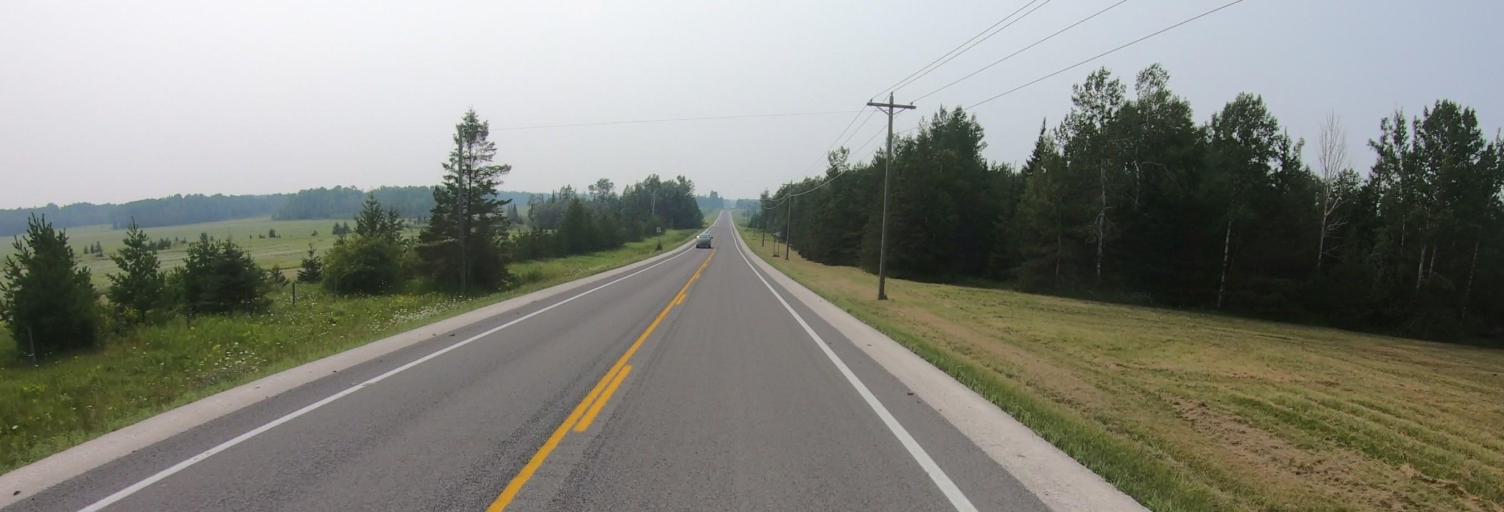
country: US
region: Michigan
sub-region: Chippewa County
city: Sault Ste. Marie
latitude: 46.0716
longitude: -84.2247
